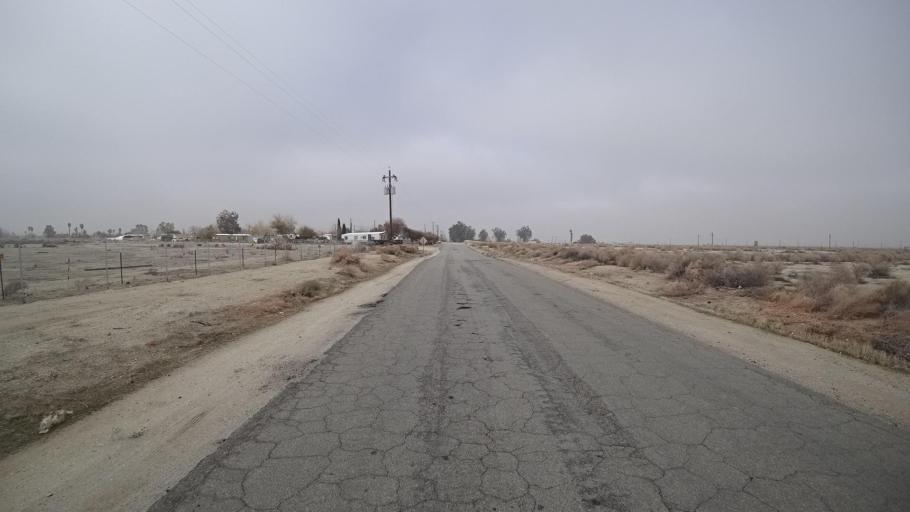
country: US
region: California
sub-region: Kern County
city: Maricopa
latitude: 35.0541
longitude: -119.3947
